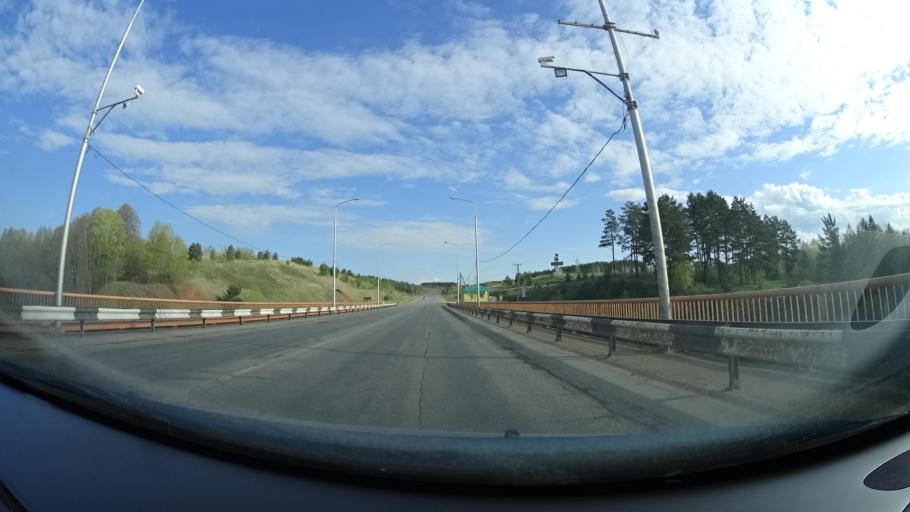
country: RU
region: Bashkortostan
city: Blagoveshchensk
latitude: 55.0719
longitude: 55.8078
